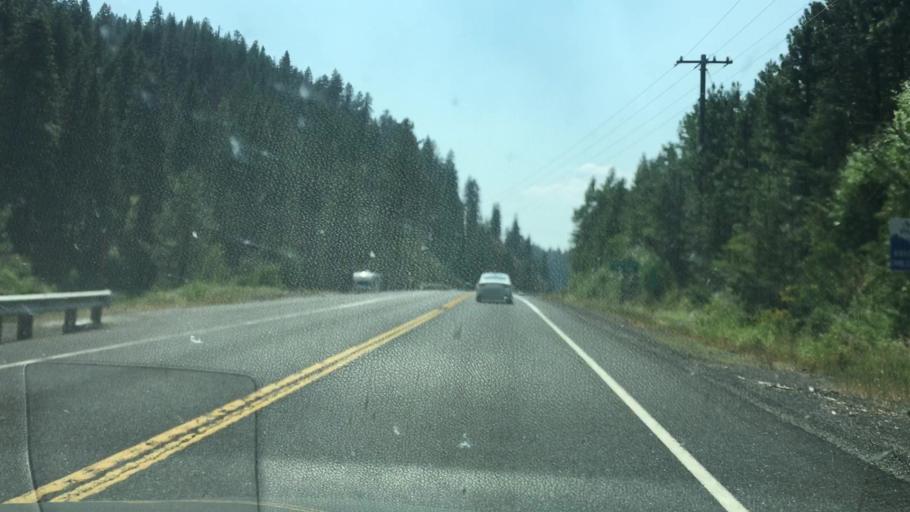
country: US
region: Idaho
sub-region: Valley County
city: McCall
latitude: 45.1250
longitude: -116.2951
